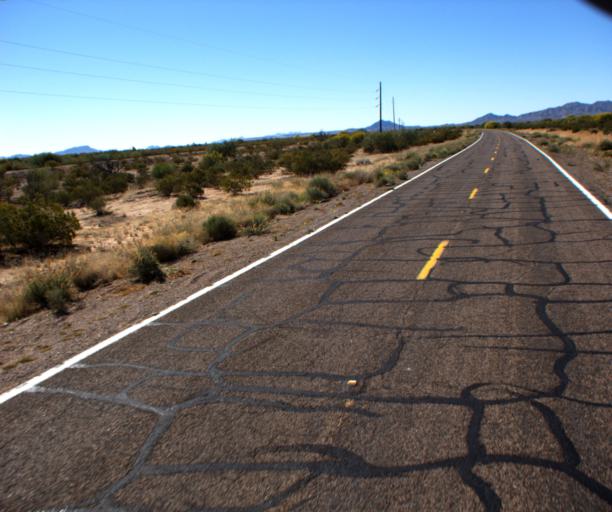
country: US
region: Arizona
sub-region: Pima County
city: Ajo
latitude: 32.4952
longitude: -112.8818
